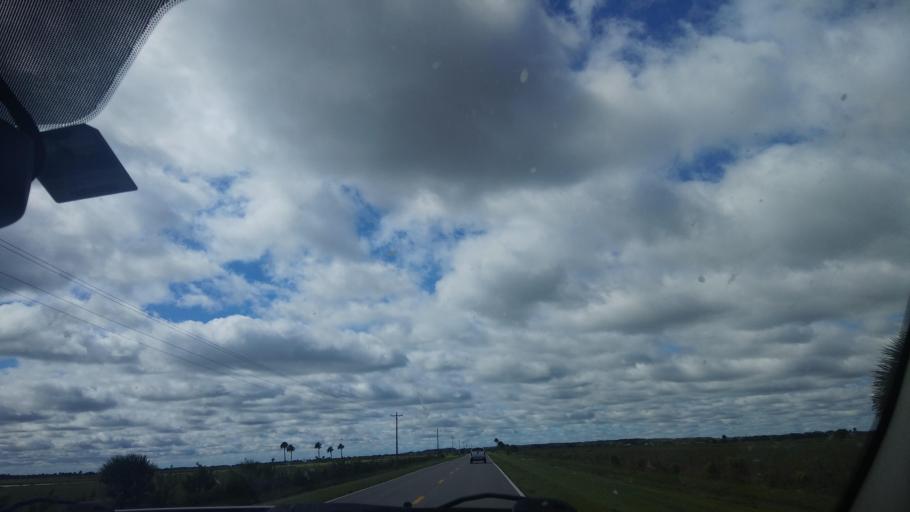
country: US
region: Florida
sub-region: Okeechobee County
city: Okeechobee
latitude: 27.3904
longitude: -80.9328
